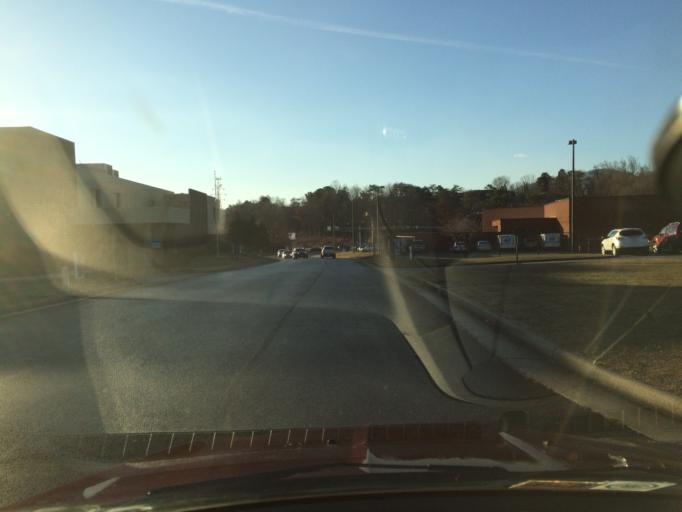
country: US
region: Virginia
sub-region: Roanoke County
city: Cave Spring
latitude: 37.2341
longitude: -80.0112
